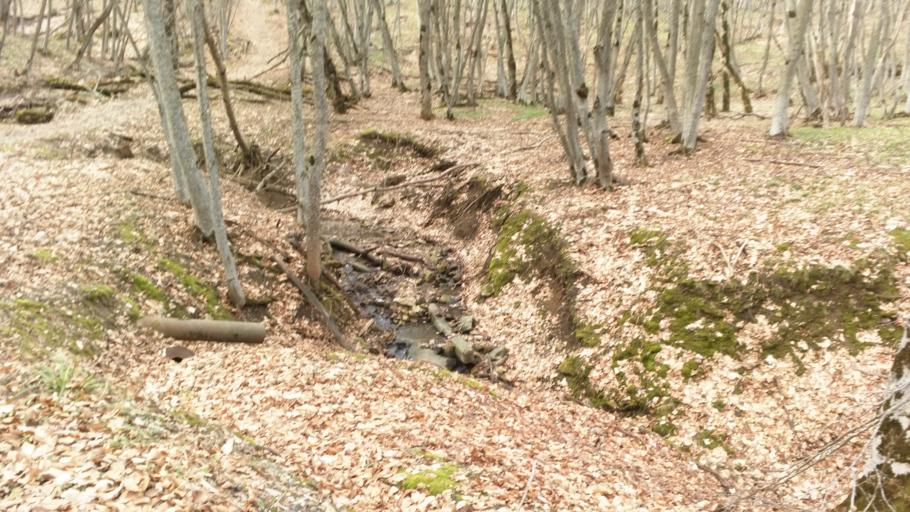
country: RU
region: Stavropol'skiy
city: Zheleznovodsk
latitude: 44.1283
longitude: 43.0246
